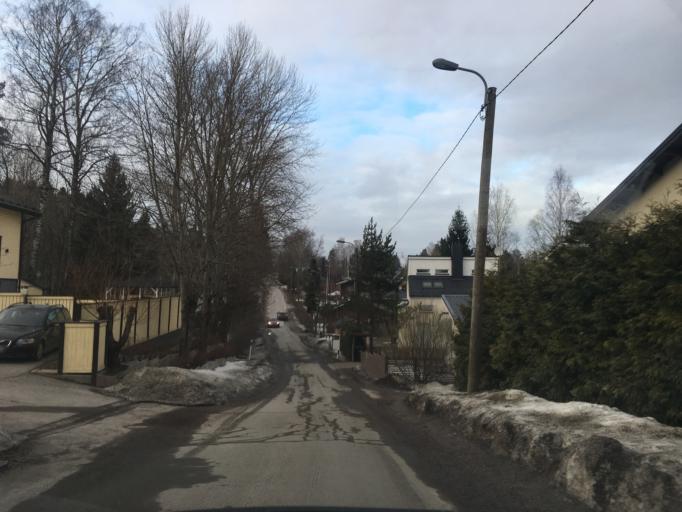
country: FI
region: Uusimaa
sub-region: Helsinki
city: Vantaa
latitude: 60.2651
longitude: 25.0892
